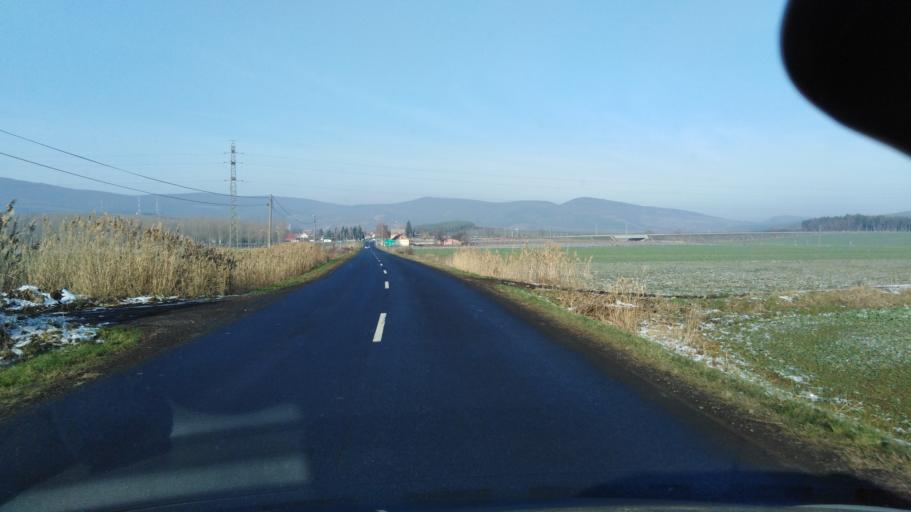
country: HU
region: Nograd
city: Paszto
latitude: 47.9408
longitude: 19.7062
